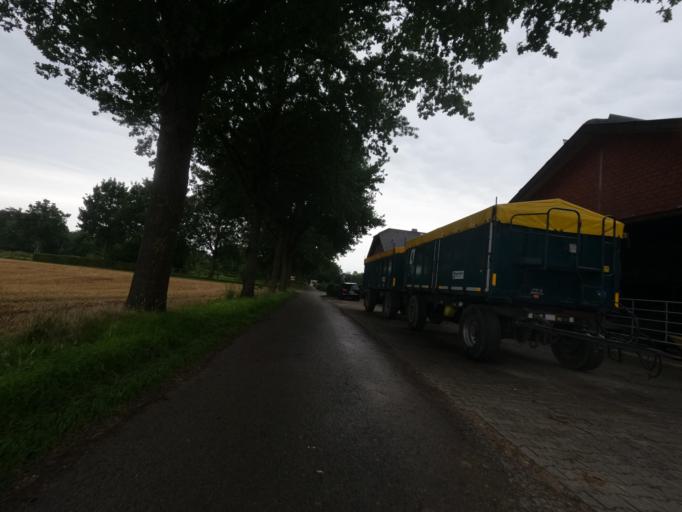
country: DE
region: North Rhine-Westphalia
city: Baesweiler
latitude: 50.9436
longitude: 6.1602
